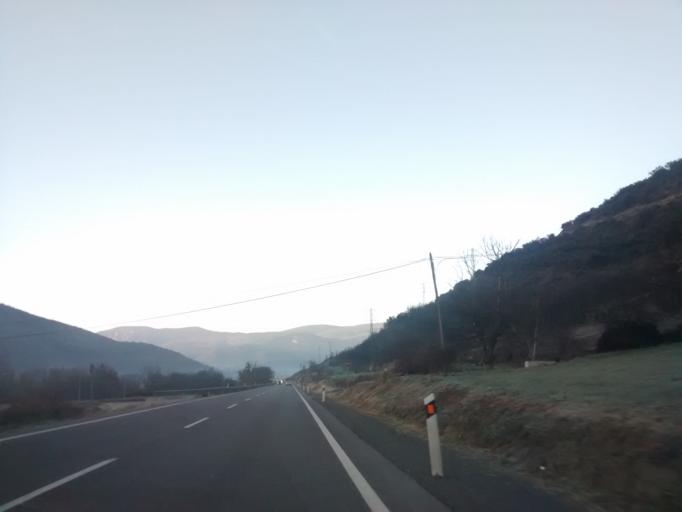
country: ES
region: Catalonia
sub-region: Provincia de Lleida
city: la Seu d'Urgell
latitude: 42.3352
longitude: 1.4116
